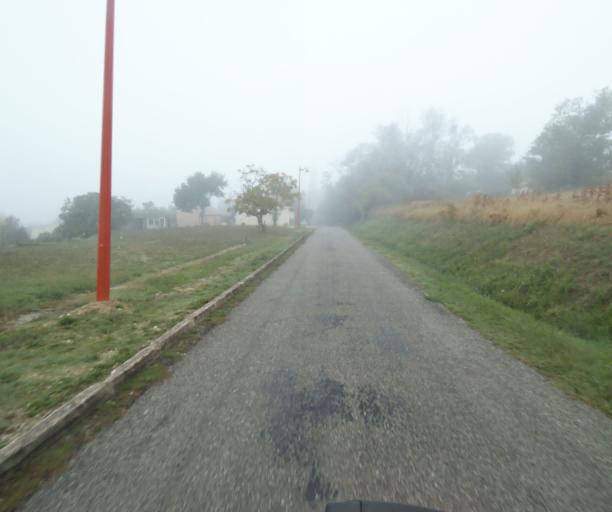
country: FR
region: Midi-Pyrenees
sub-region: Departement du Tarn-et-Garonne
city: Nohic
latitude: 43.9210
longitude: 1.4728
